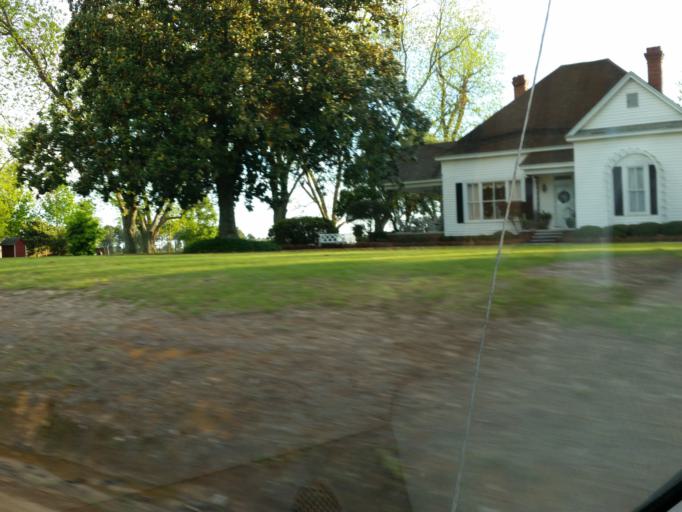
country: US
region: Georgia
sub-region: Turner County
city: Ashburn
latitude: 31.6330
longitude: -83.6141
